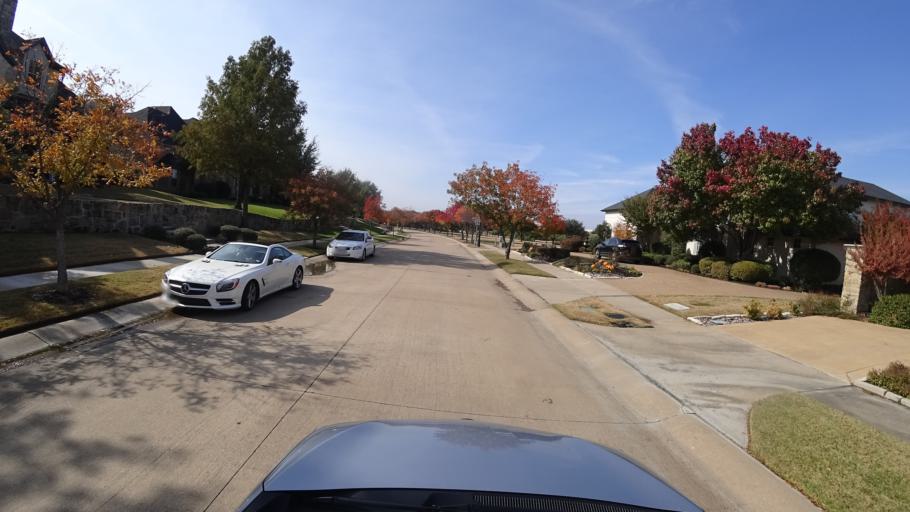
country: US
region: Texas
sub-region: Denton County
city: The Colony
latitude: 33.0418
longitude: -96.8949
